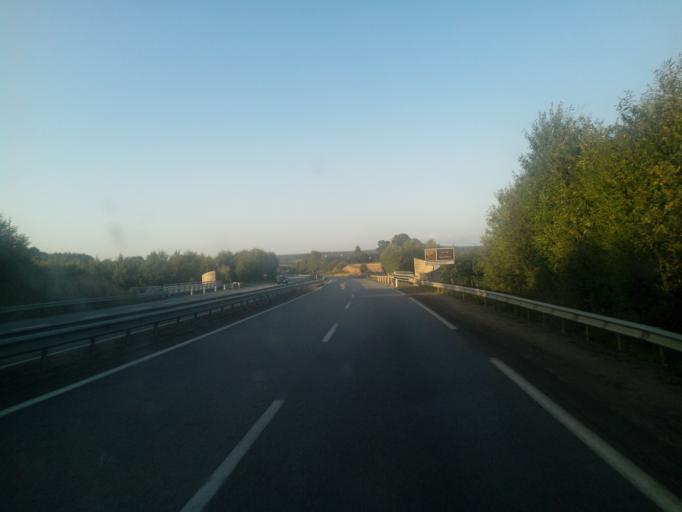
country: FR
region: Brittany
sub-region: Departement des Cotes-d'Armor
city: Loudeac
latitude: 48.1678
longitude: -2.7355
